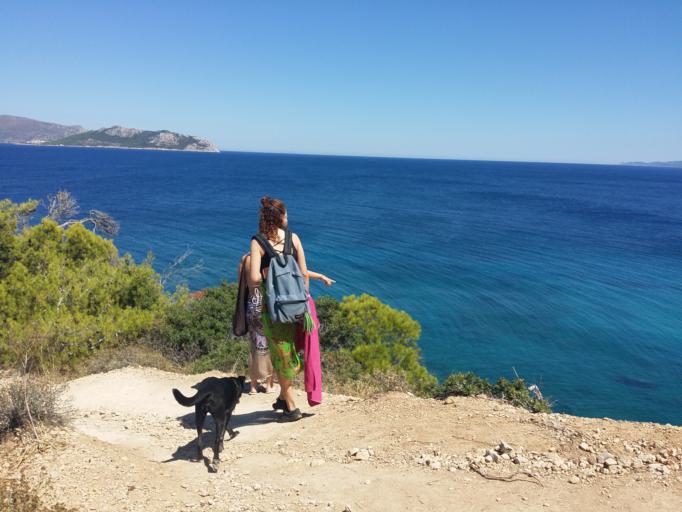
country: GR
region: Attica
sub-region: Nomos Piraios
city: Megalochori
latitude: 37.7015
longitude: 23.3729
